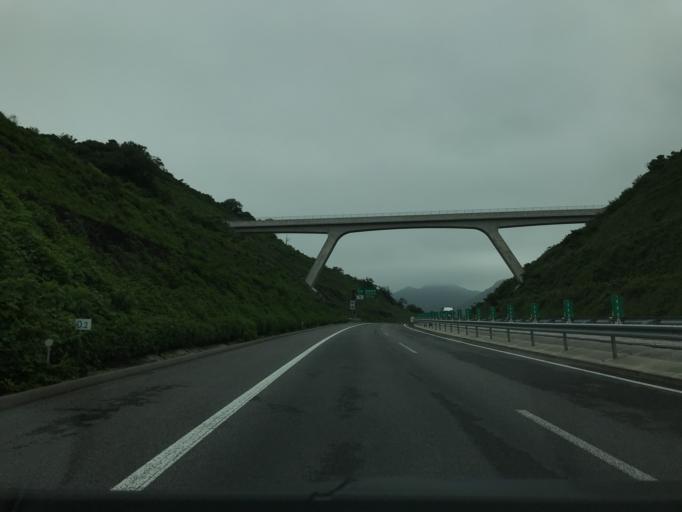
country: JP
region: Oita
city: Bungo-Takada-shi
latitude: 33.5041
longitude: 131.3070
